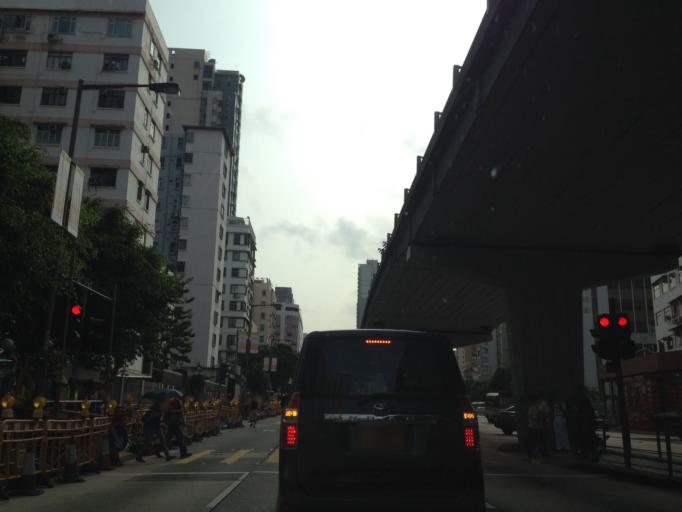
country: HK
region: Kowloon City
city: Kowloon
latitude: 22.3272
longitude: 114.1871
